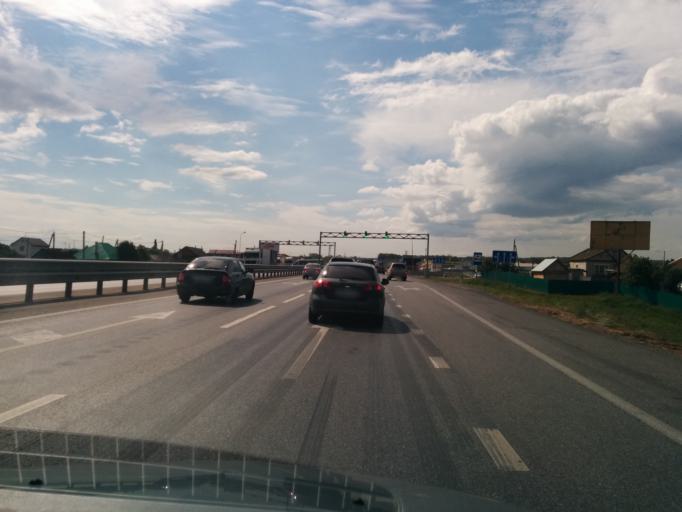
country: RU
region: Bashkortostan
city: Avdon
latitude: 54.5024
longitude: 55.9026
